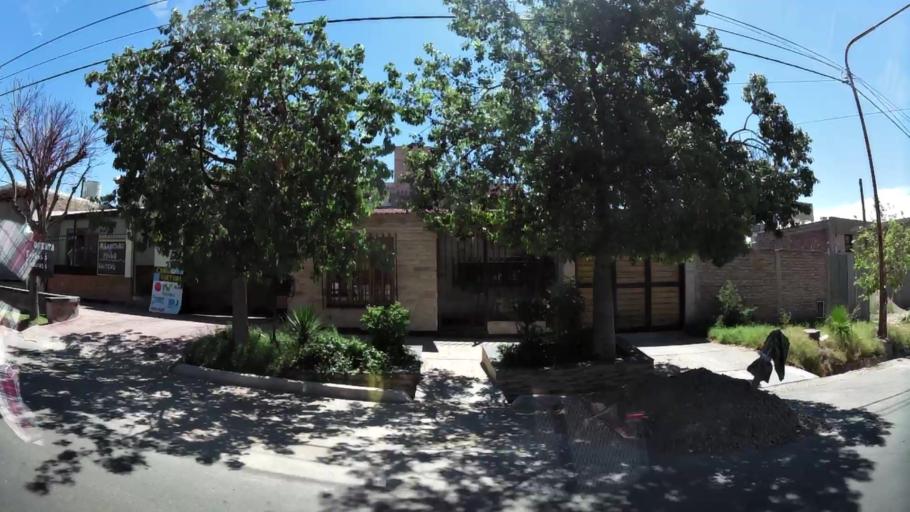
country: AR
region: Mendoza
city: Las Heras
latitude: -32.8475
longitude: -68.8719
